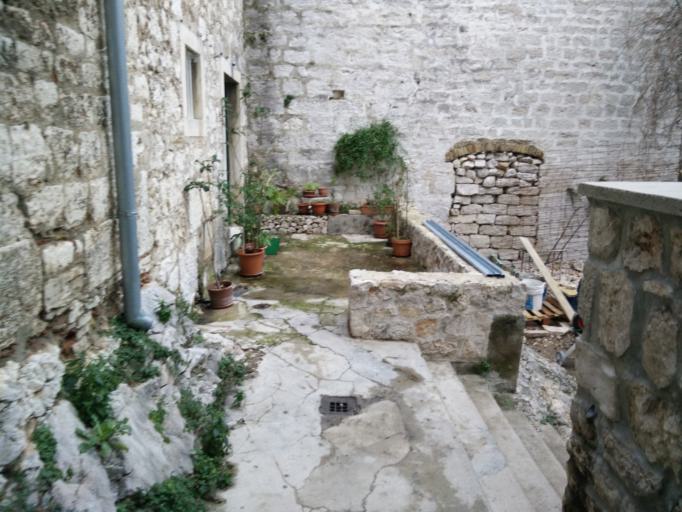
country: HR
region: Sibensko-Kniniska
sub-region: Grad Sibenik
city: Sibenik
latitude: 43.7382
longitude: 15.8882
